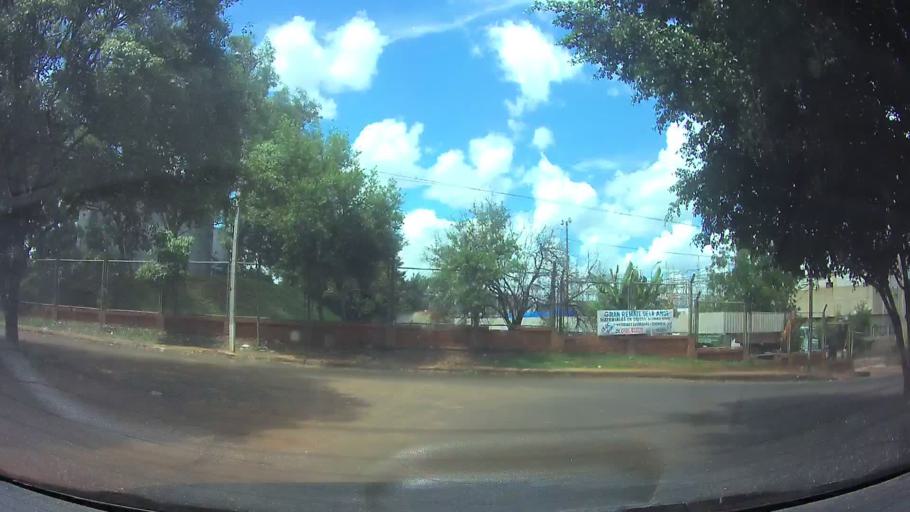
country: PY
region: Central
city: San Lorenzo
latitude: -25.3223
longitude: -57.5107
